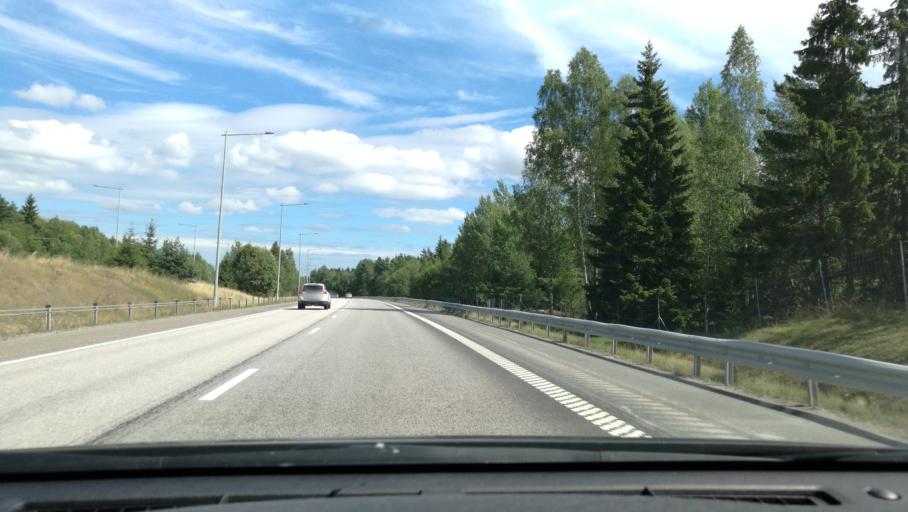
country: SE
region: Stockholm
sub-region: Upplands-Bro Kommun
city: Kungsaengen
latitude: 59.5098
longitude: 17.6961
